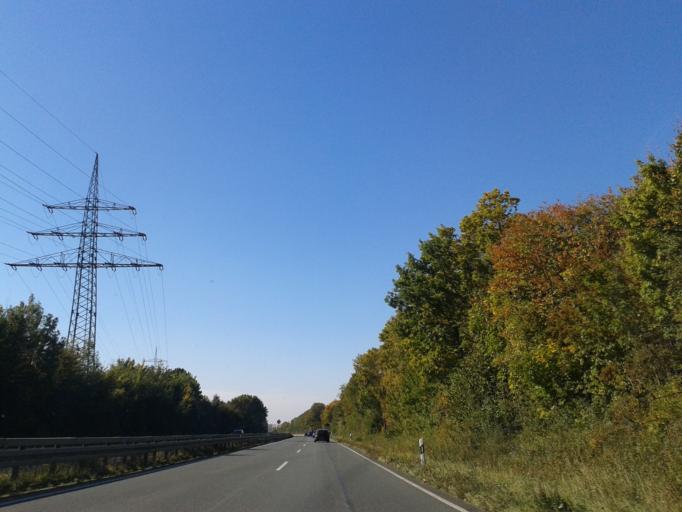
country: DE
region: North Rhine-Westphalia
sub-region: Regierungsbezirk Detmold
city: Paderborn
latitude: 51.7008
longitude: 8.7557
